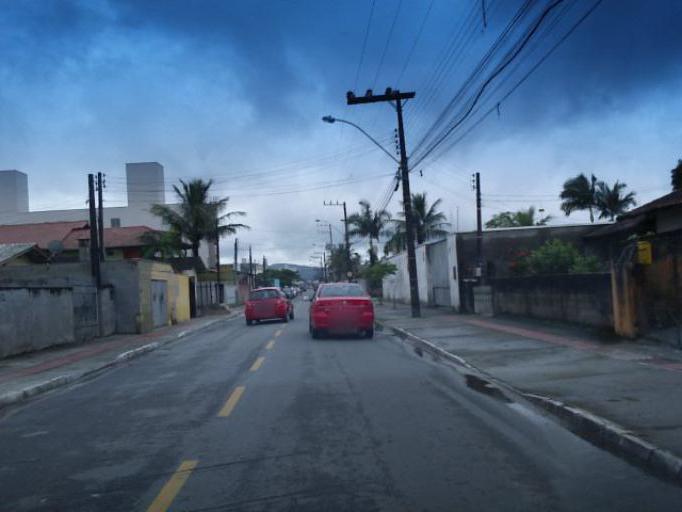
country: BR
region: Santa Catarina
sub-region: Itajai
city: Itajai
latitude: -26.8964
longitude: -48.7020
